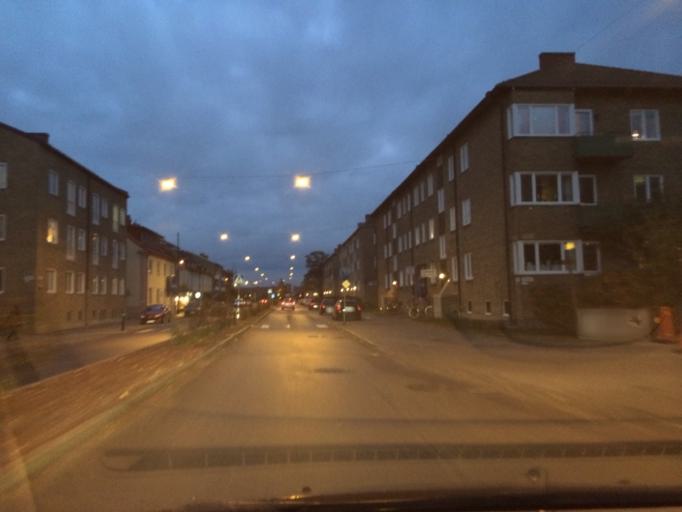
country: SE
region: Skane
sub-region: Malmo
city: Bunkeflostrand
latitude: 55.5812
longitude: 12.9378
